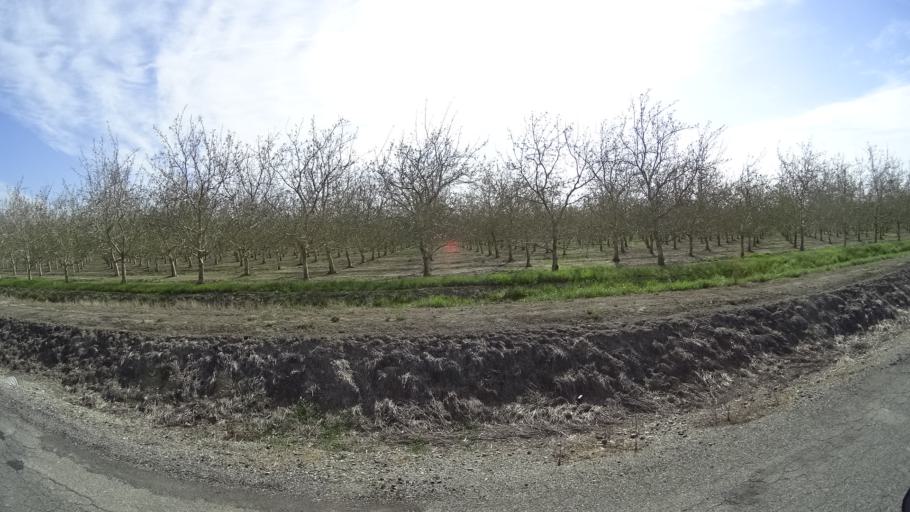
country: US
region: California
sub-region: Glenn County
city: Hamilton City
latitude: 39.6218
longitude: -122.0463
